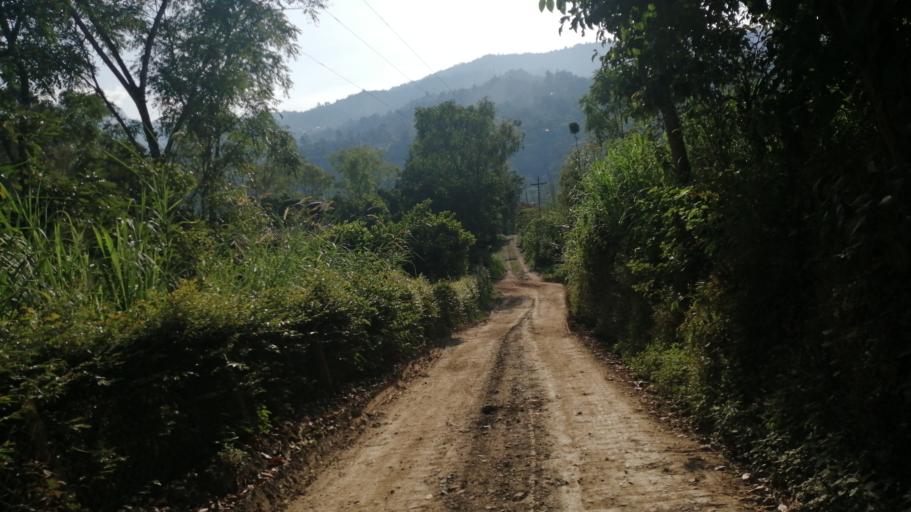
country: CO
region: Boyaca
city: Garagoa
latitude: 5.0800
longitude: -73.3902
